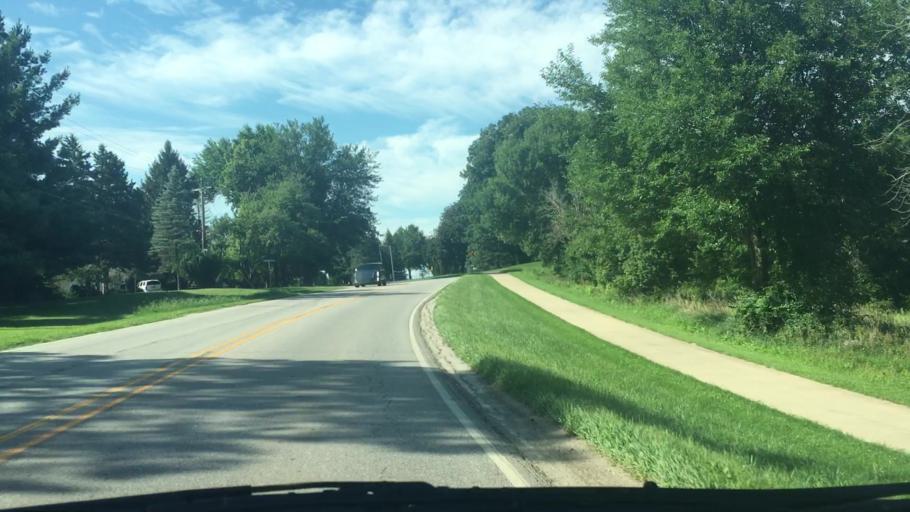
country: US
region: Iowa
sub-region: Johnson County
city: Coralville
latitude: 41.7087
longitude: -91.5501
